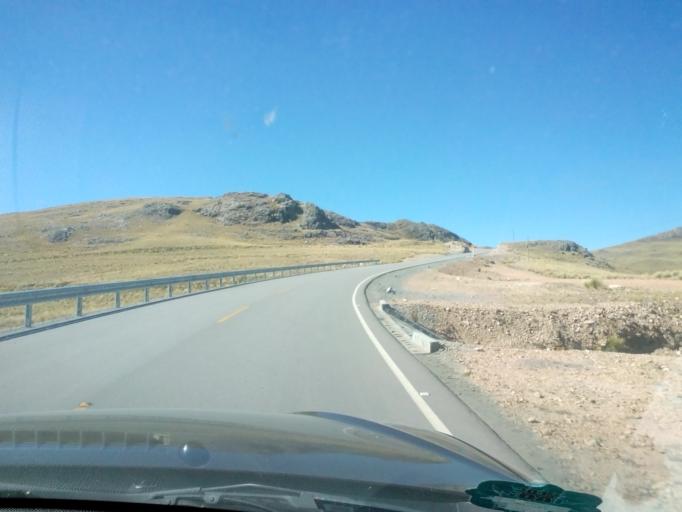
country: PE
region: Ayacucho
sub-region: Provincia de Huamanga
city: Acocro
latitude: -13.3618
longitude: -74.0843
